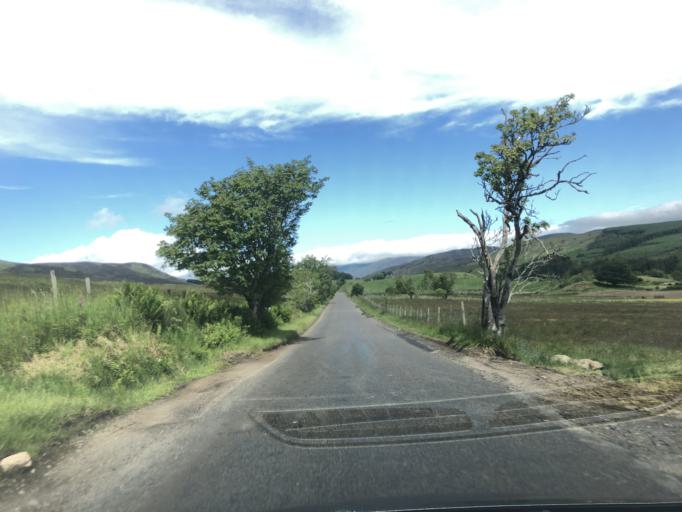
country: GB
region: Scotland
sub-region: Angus
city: Kirriemuir
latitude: 56.7493
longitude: -3.0142
